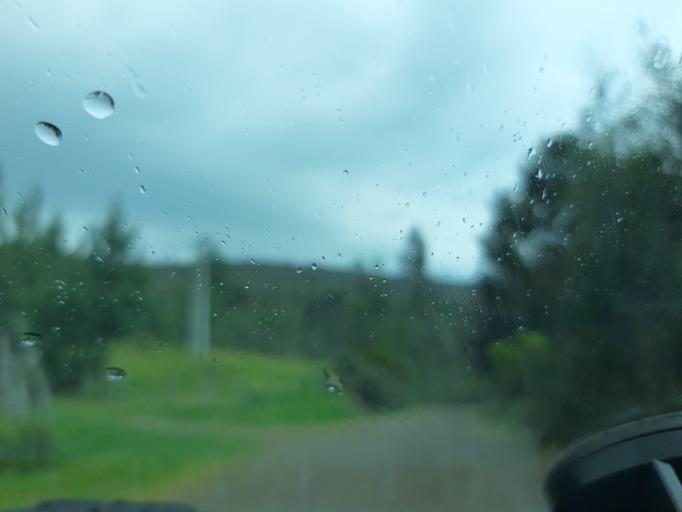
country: CO
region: Boyaca
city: Raquira
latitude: 5.5067
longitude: -73.6876
